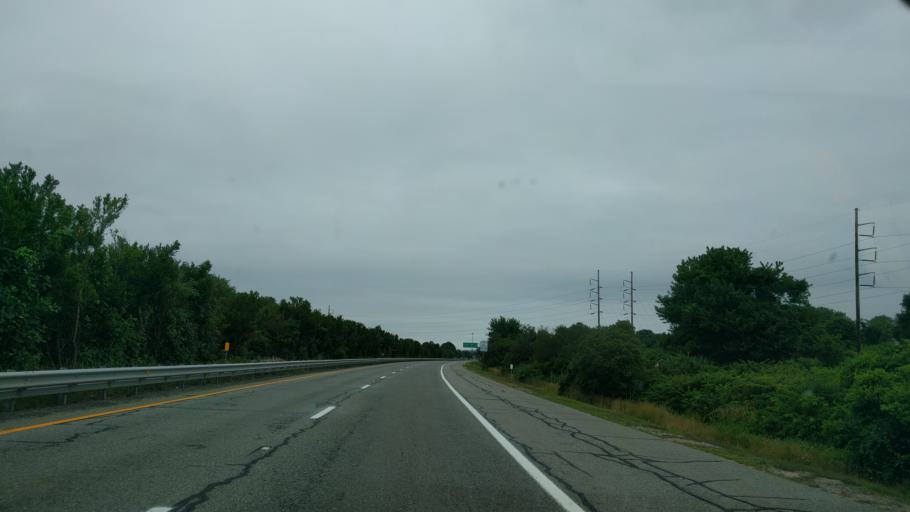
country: US
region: Rhode Island
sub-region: Newport County
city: Portsmouth
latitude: 41.6229
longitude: -71.2497
